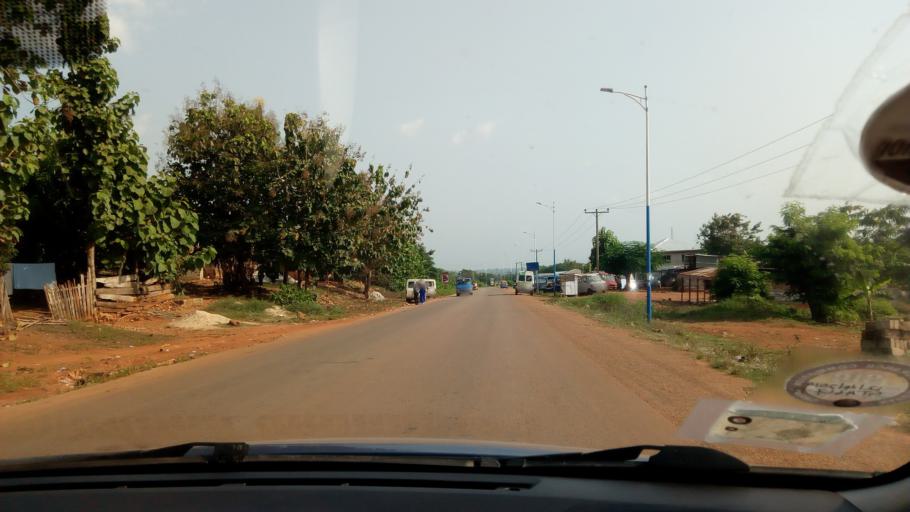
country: GH
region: Western
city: Bibiani
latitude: 6.8029
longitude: -2.5231
